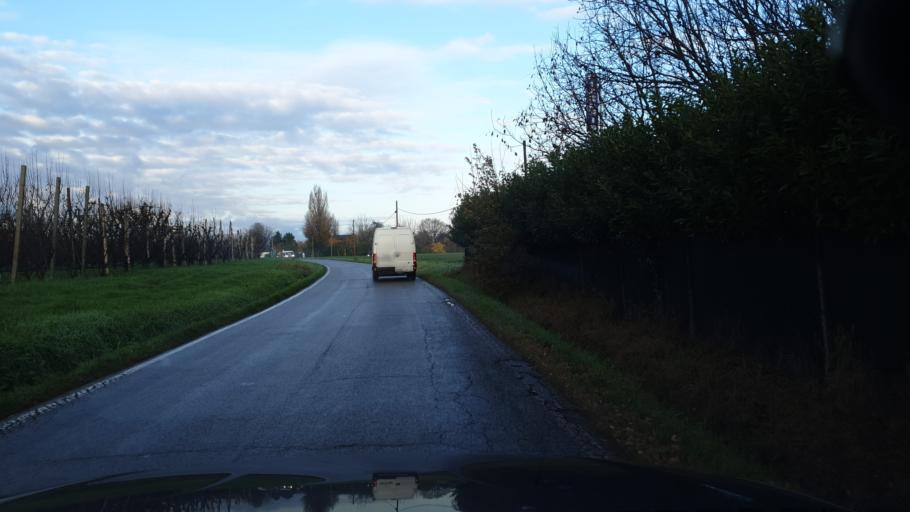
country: IT
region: Emilia-Romagna
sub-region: Provincia di Bologna
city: Crespellano
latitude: 44.5220
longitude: 11.1206
